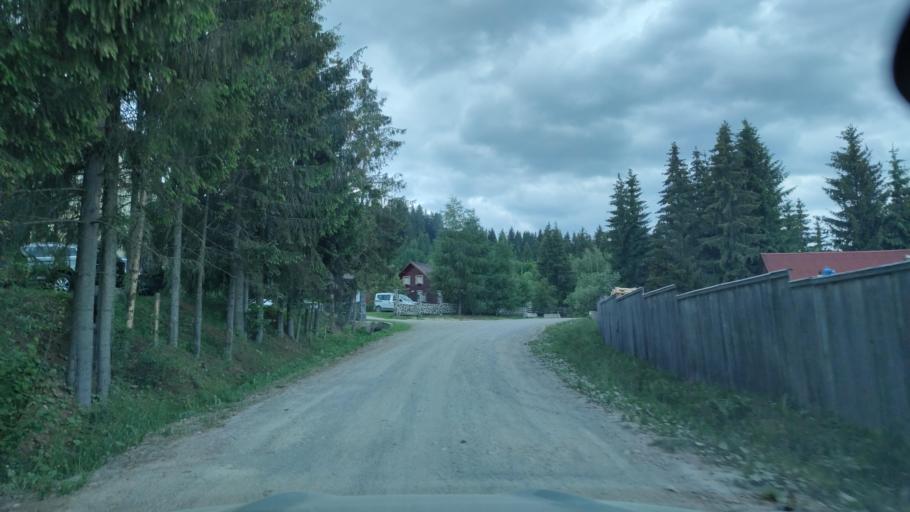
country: RO
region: Harghita
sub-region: Comuna Joseni
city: Joseni
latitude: 46.6683
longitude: 25.3761
